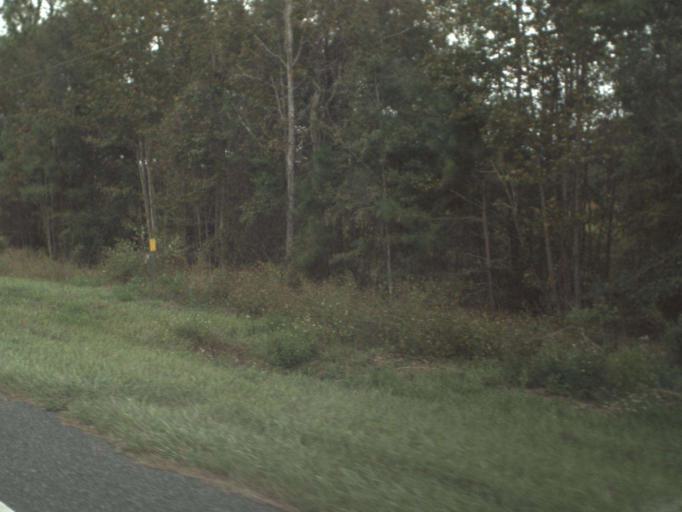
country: US
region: Florida
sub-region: Leon County
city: Woodville
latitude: 30.4057
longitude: -84.0594
